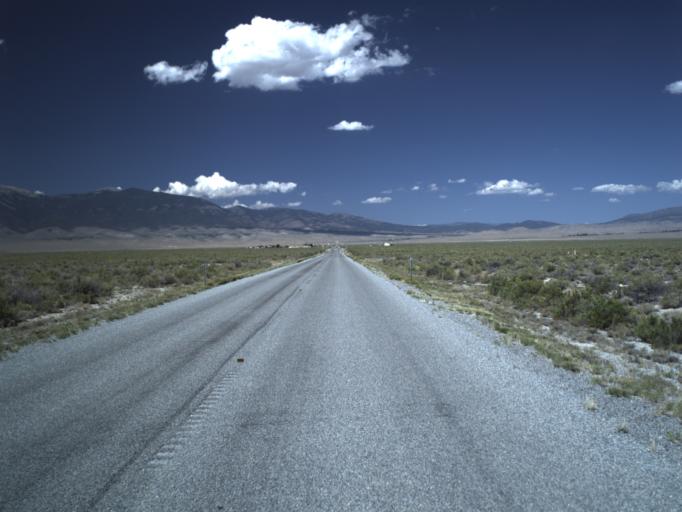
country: US
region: Nevada
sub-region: White Pine County
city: McGill
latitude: 39.0552
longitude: -114.0236
